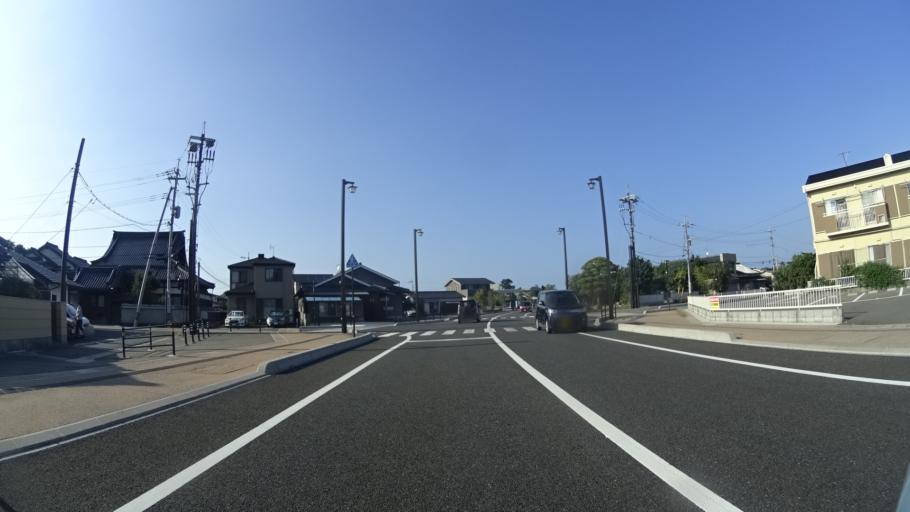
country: JP
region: Yamaguchi
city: Hagi
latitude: 34.4081
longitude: 131.3914
